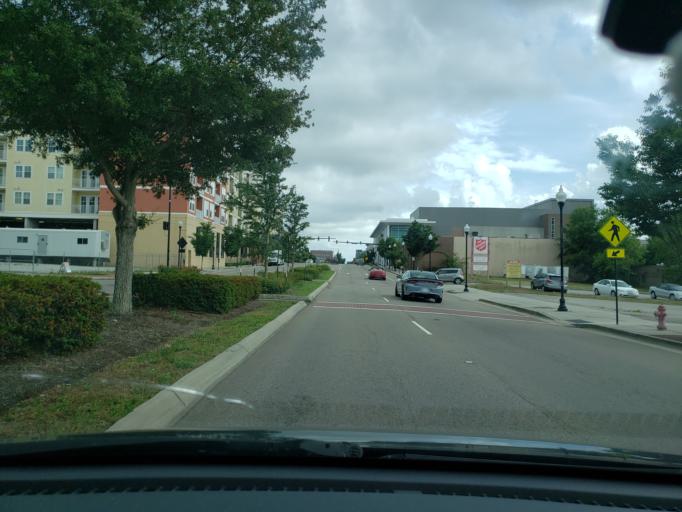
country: US
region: North Carolina
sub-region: New Hanover County
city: Wilmington
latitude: 34.2458
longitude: -77.9473
